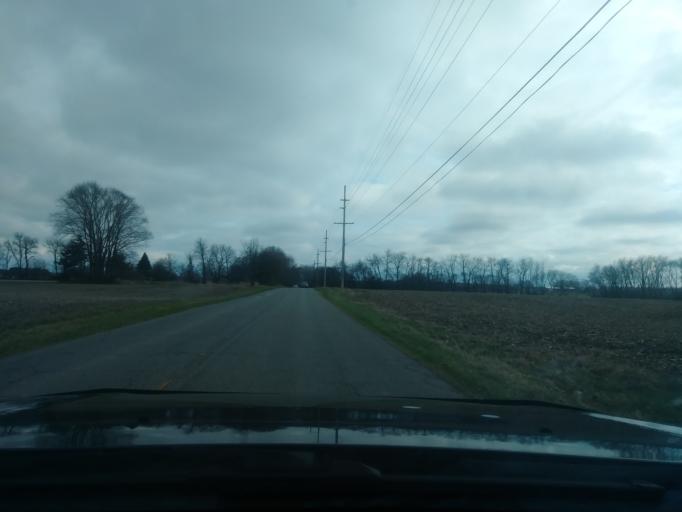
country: US
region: Indiana
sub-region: LaPorte County
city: LaPorte
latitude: 41.6203
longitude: -86.7964
